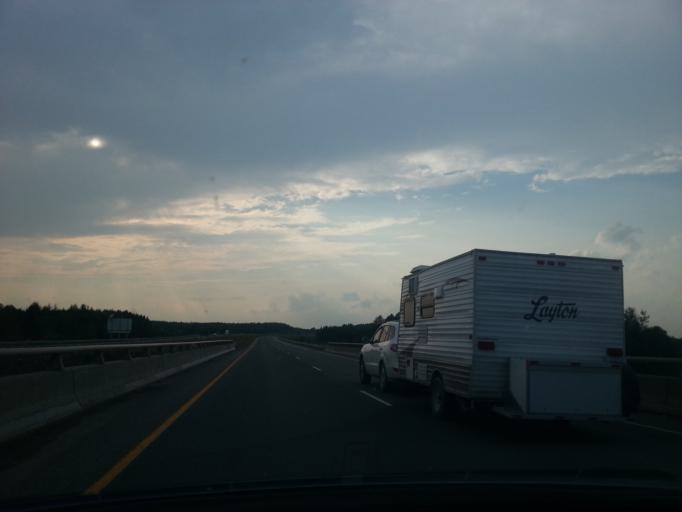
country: CA
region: New Brunswick
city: Harrison Brook
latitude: 47.2891
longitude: -68.0414
